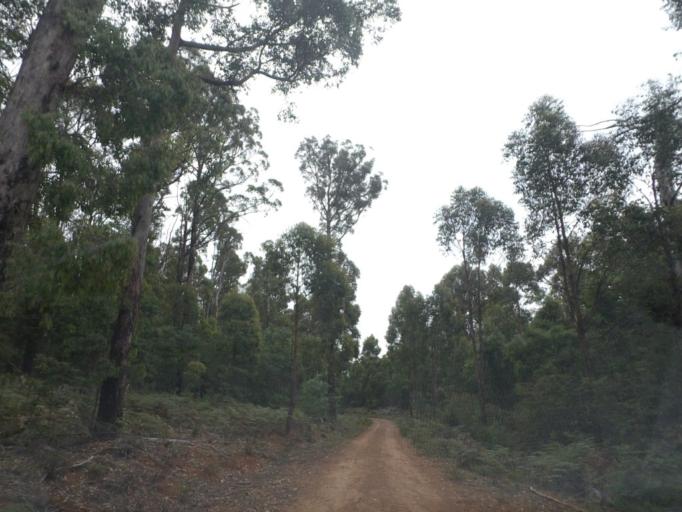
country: AU
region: Victoria
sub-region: Murrindindi
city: Alexandra
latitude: -37.3912
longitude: 145.5775
